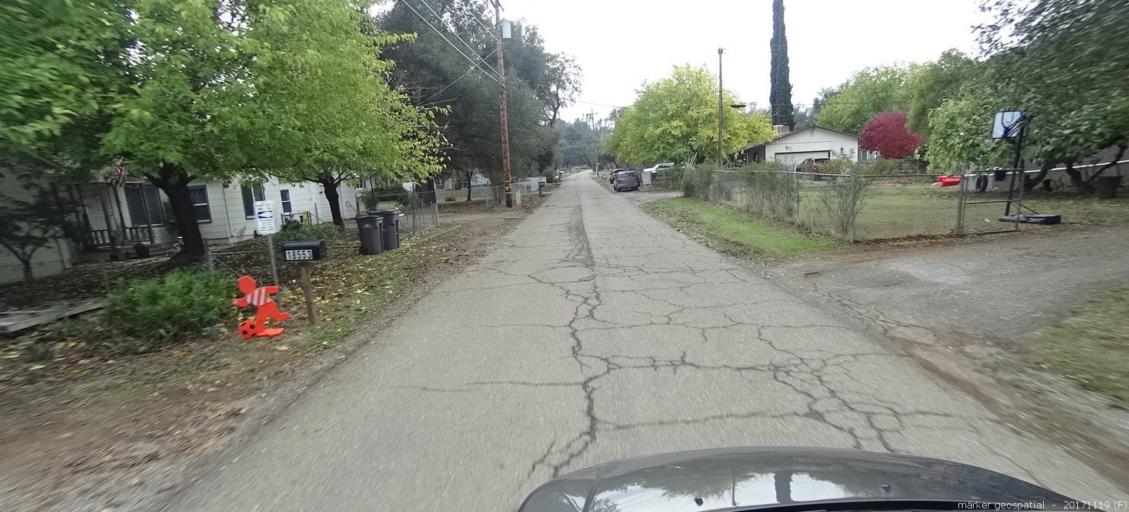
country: US
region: California
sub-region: Shasta County
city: Anderson
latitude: 40.4888
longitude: -122.3672
